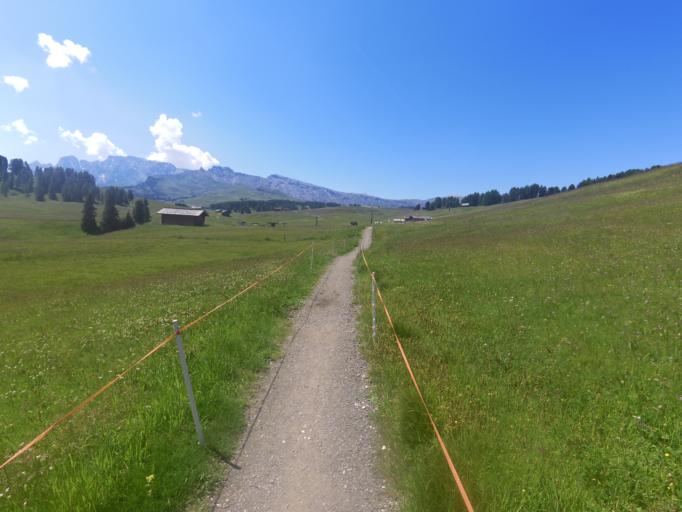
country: IT
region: Trentino-Alto Adige
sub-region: Bolzano
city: Ortisei
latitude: 46.5495
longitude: 11.6582
